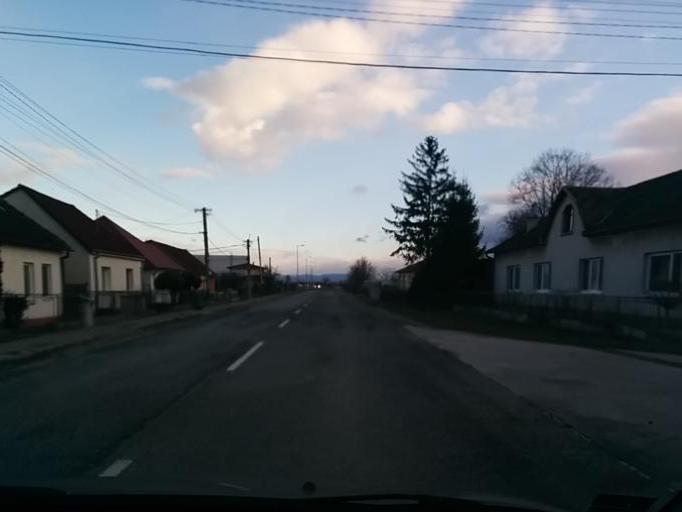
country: SK
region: Nitriansky
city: Cachtice
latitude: 48.6889
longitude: 17.8479
